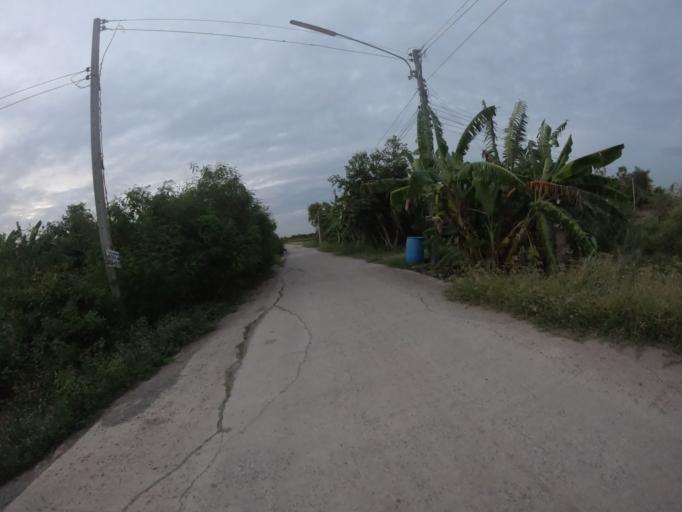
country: TH
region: Pathum Thani
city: Ban Lam Luk Ka
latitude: 14.0157
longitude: 100.8019
